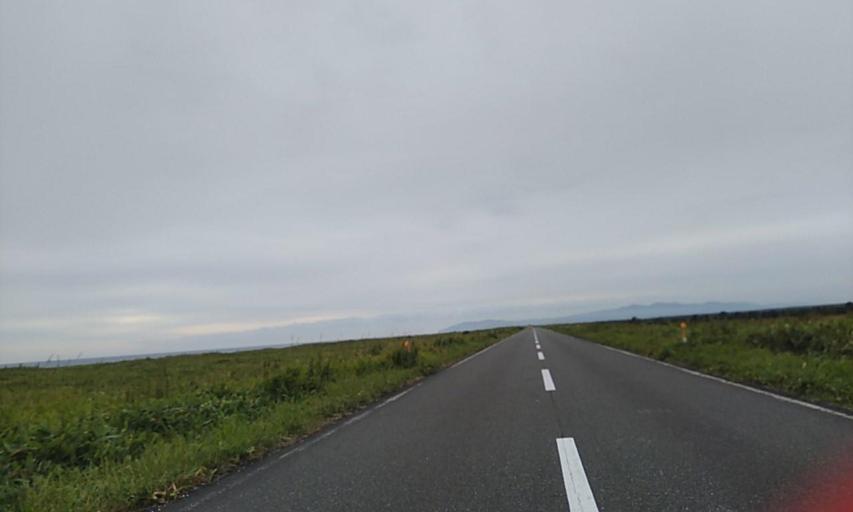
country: JP
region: Hokkaido
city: Makubetsu
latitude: 45.2659
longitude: 142.2411
